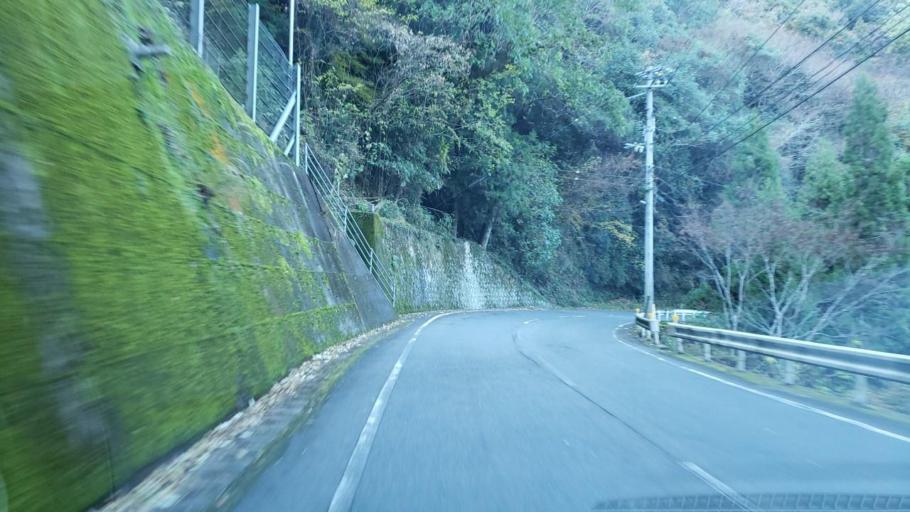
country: JP
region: Tokushima
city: Wakimachi
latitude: 34.0128
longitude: 134.0316
